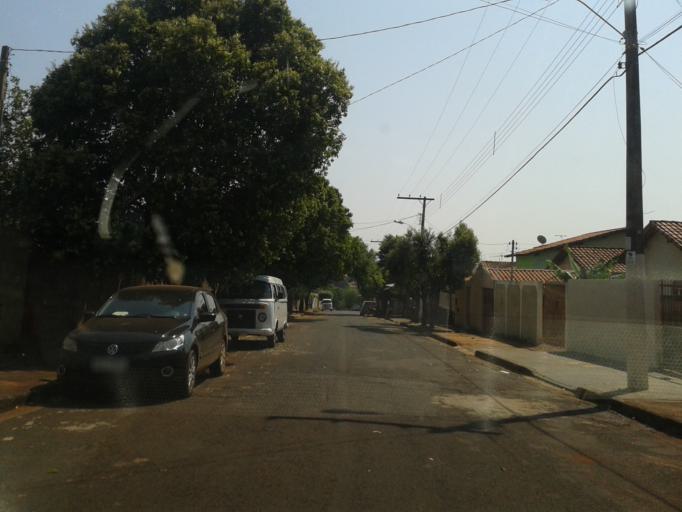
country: BR
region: Minas Gerais
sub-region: Ituiutaba
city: Ituiutaba
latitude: -18.9780
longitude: -49.4878
